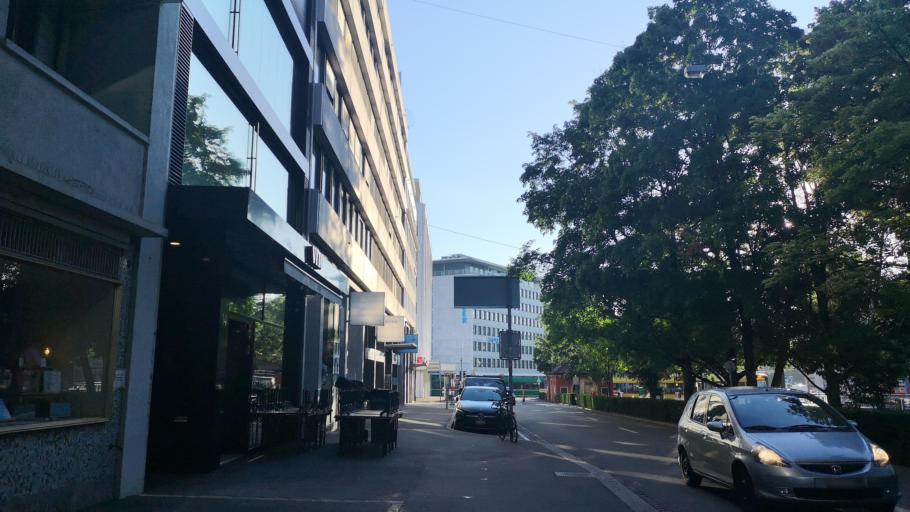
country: CH
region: Basel-City
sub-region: Basel-Stadt
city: Basel
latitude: 47.5506
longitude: 7.5934
